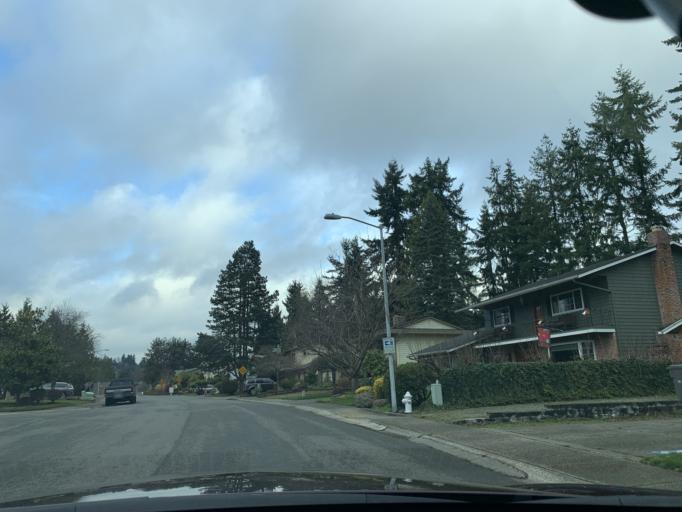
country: US
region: Washington
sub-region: King County
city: Kingsgate
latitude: 47.7396
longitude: -122.1846
